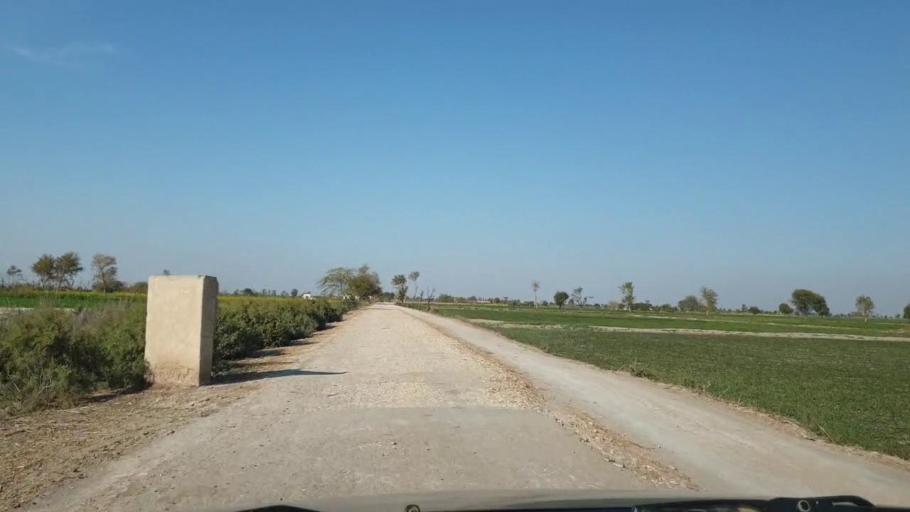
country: PK
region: Sindh
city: Khadro
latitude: 26.1556
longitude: 68.7536
